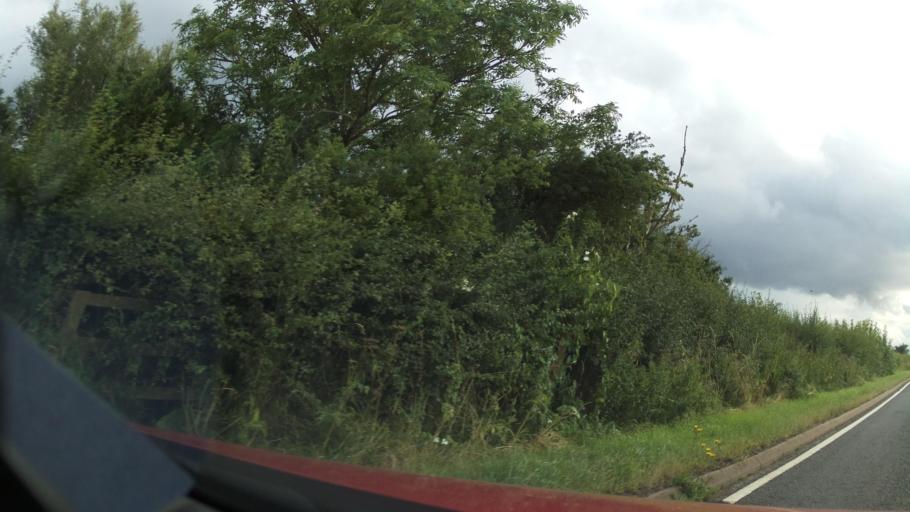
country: GB
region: England
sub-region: Warwickshire
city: Dunchurch
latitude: 52.3026
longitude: -1.3170
